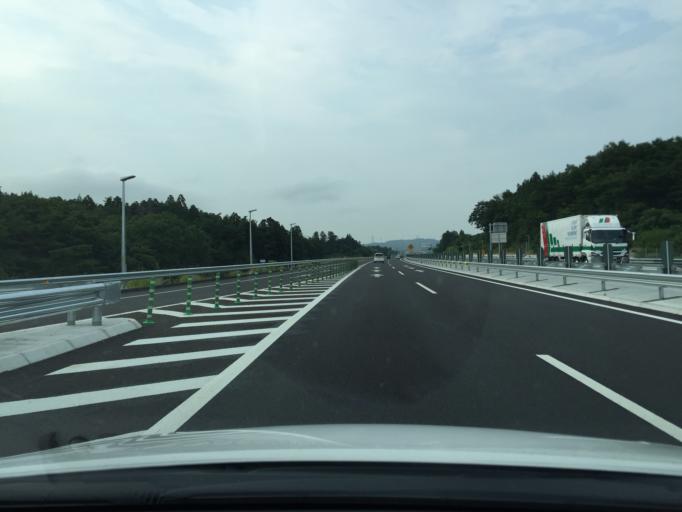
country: JP
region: Fukushima
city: Namie
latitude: 37.3762
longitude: 140.9662
